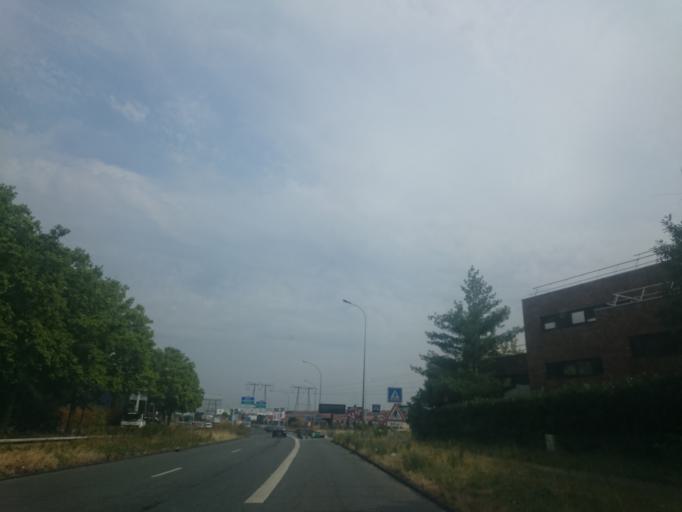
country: FR
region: Ile-de-France
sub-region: Departement du Val-de-Marne
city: Rungis
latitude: 48.7482
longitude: 2.3684
